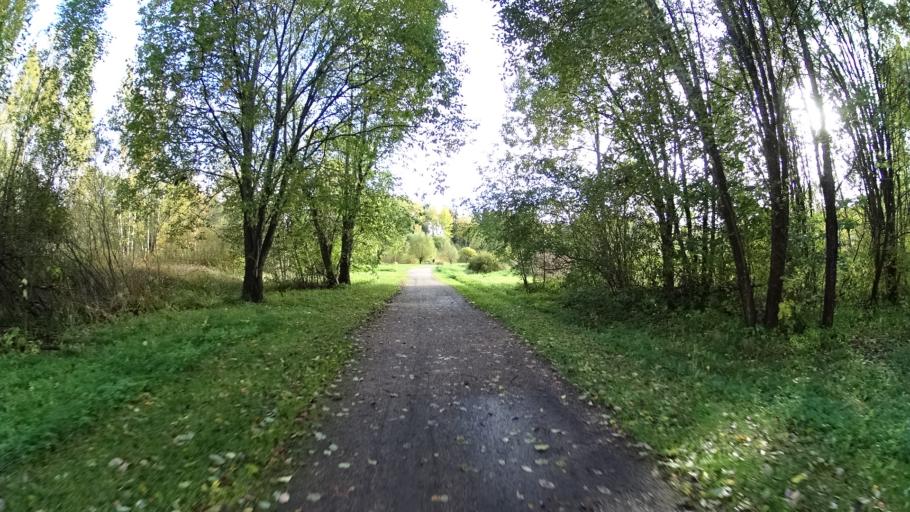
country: FI
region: Uusimaa
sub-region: Helsinki
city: Kilo
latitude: 60.2738
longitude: 24.8164
